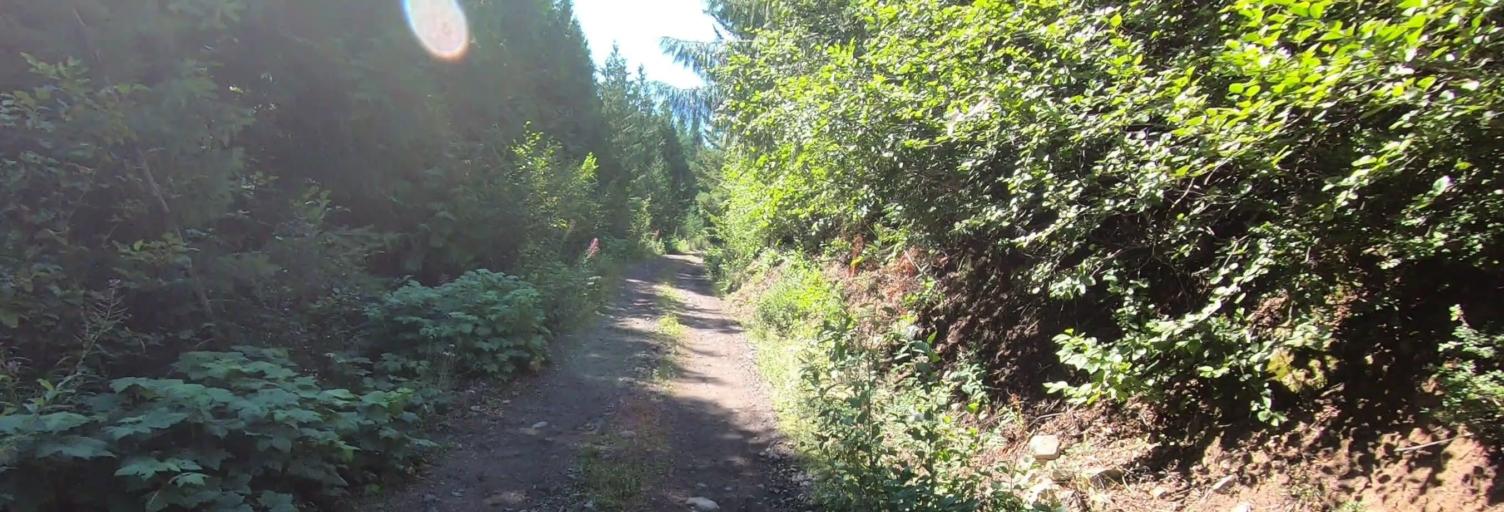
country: CA
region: British Columbia
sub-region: Fraser Valley Regional District
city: Chilliwack
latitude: 48.8591
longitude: -121.7799
